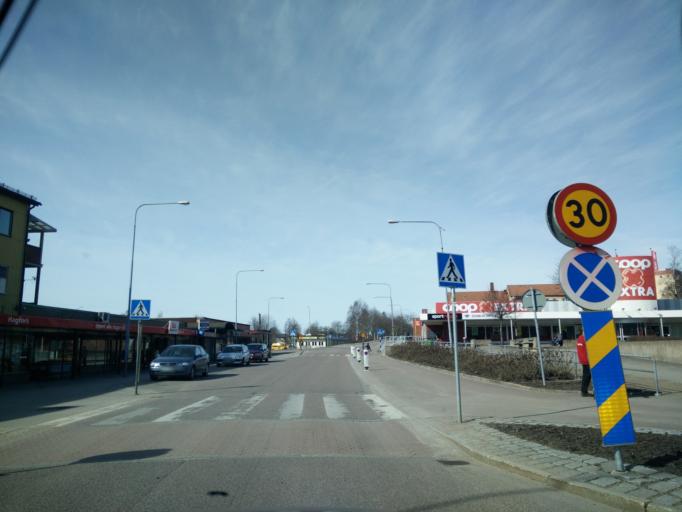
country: SE
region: Vaermland
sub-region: Hagfors Kommun
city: Hagfors
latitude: 60.0343
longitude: 13.6963
